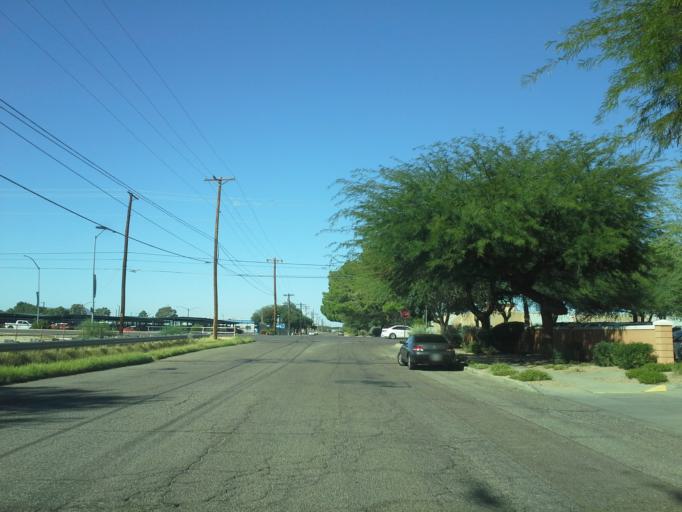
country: US
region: Arizona
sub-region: Pima County
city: Summit
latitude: 32.1268
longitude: -110.9337
